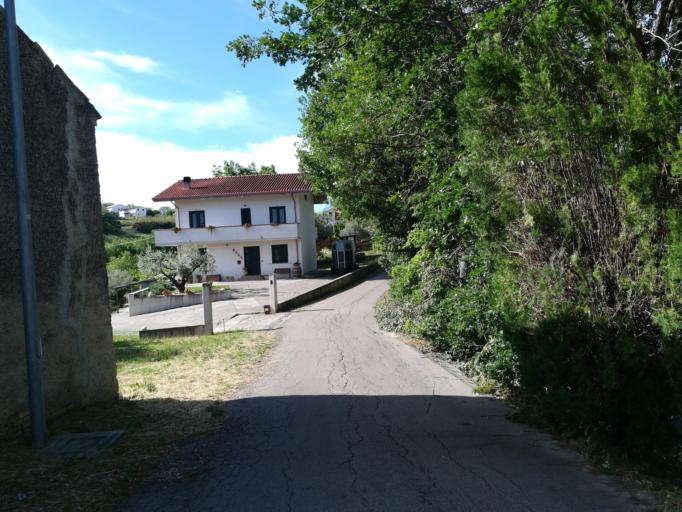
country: IT
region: Abruzzo
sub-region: Provincia di Chieti
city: Bucchianico
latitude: 42.2921
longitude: 14.1674
